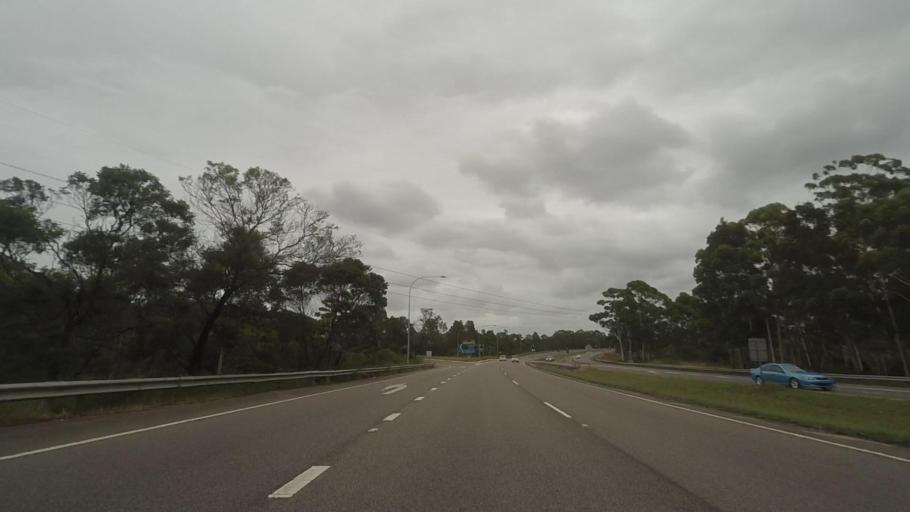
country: AU
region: New South Wales
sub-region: Wyong Shire
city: Buff Point
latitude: -33.2054
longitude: 151.5175
